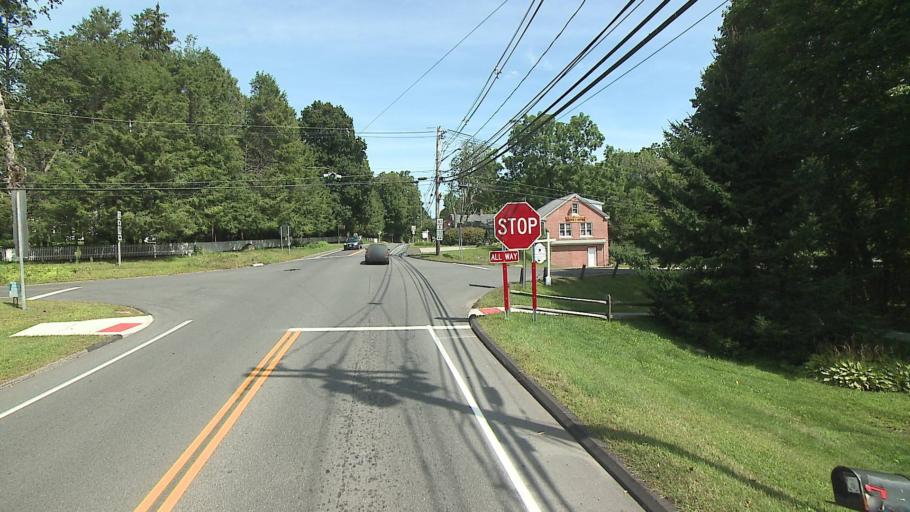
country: US
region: Connecticut
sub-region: Litchfield County
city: Bethlehem Village
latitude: 41.6393
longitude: -73.2083
